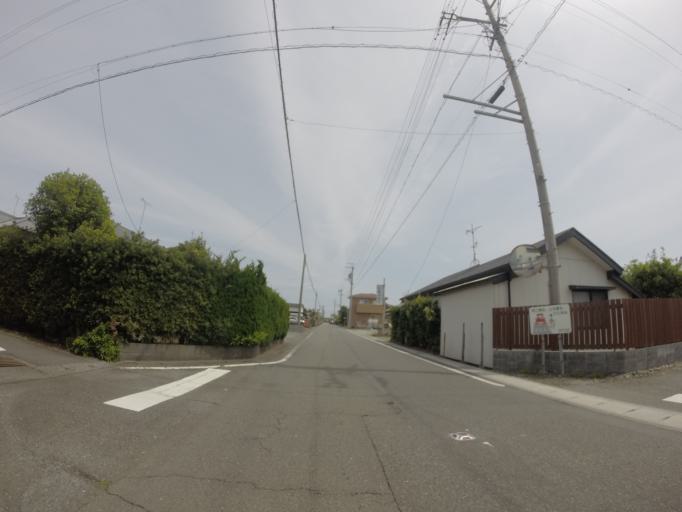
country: JP
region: Shizuoka
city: Yaizu
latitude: 34.7950
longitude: 138.3081
